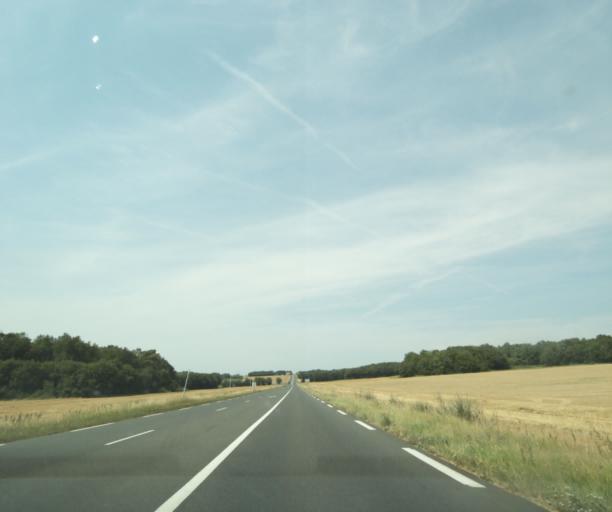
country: FR
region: Centre
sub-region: Departement d'Indre-et-Loire
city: Sainte-Maure-de-Touraine
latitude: 47.0786
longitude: 0.6128
